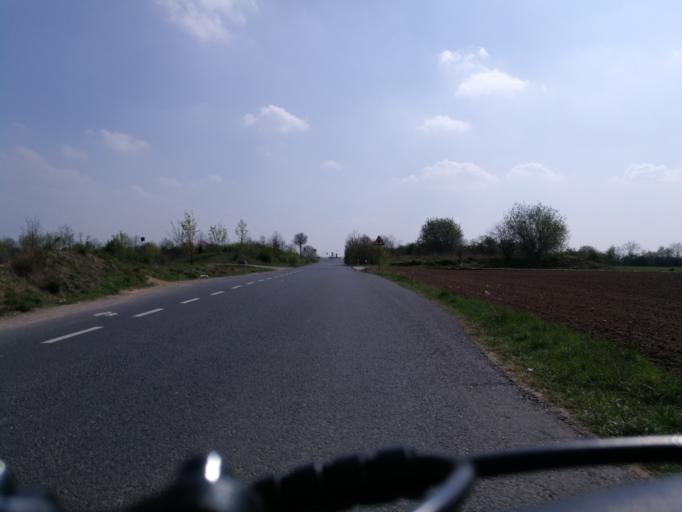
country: DE
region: North Rhine-Westphalia
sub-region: Regierungsbezirk Dusseldorf
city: Dusseldorf
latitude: 51.1386
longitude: 6.7562
